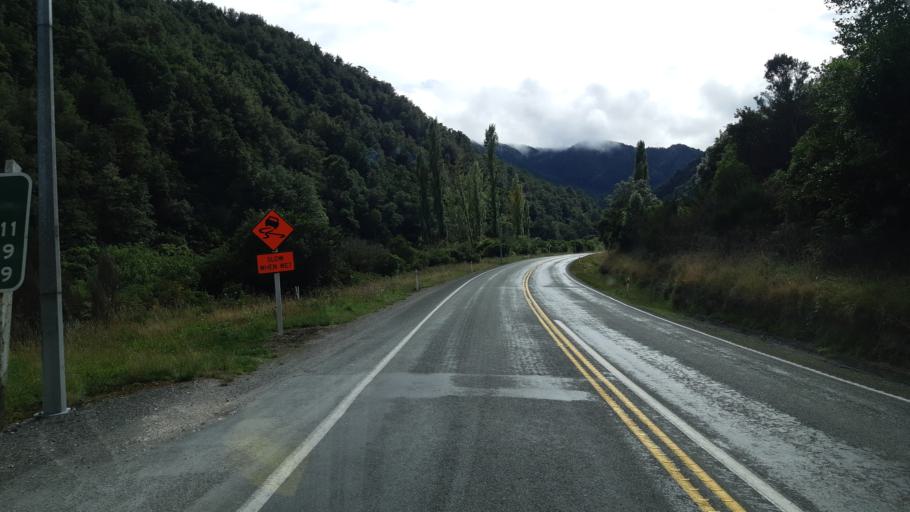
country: NZ
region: West Coast
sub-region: Buller District
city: Westport
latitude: -41.7774
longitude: 172.2196
